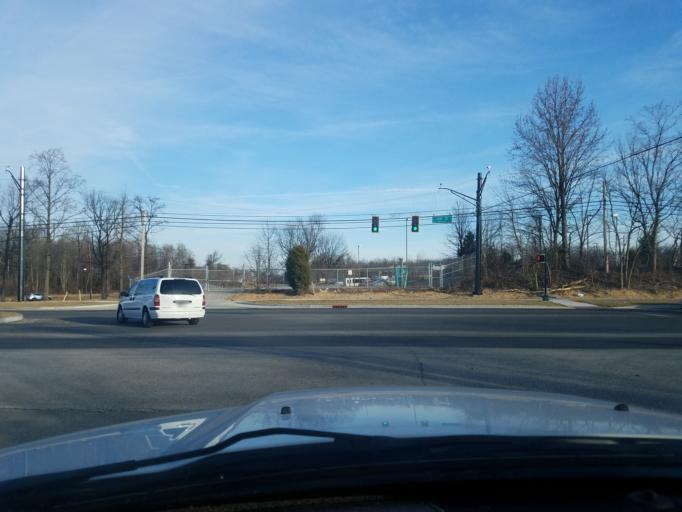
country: US
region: Indiana
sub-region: Clark County
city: Oak Park
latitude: 38.3280
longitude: -85.7120
